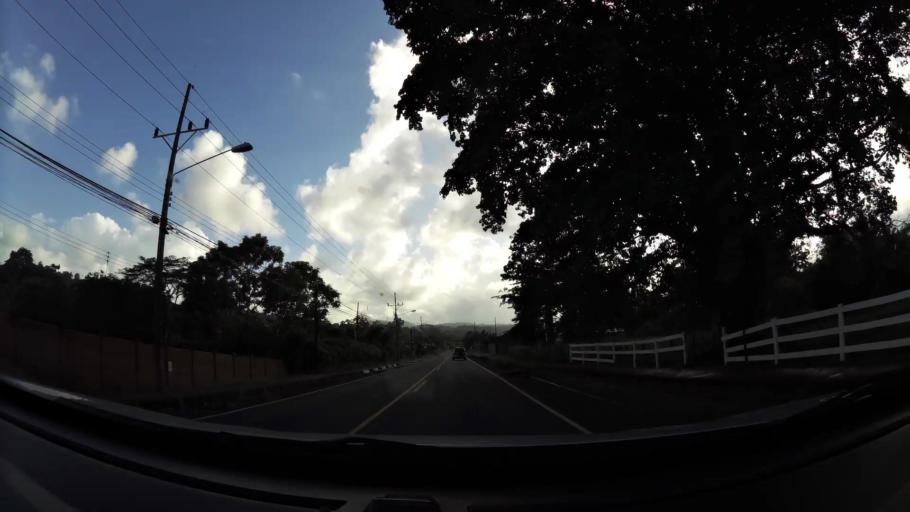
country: CR
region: Limon
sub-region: Canton de Siquirres
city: Siquirres
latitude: 10.0910
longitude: -83.5408
